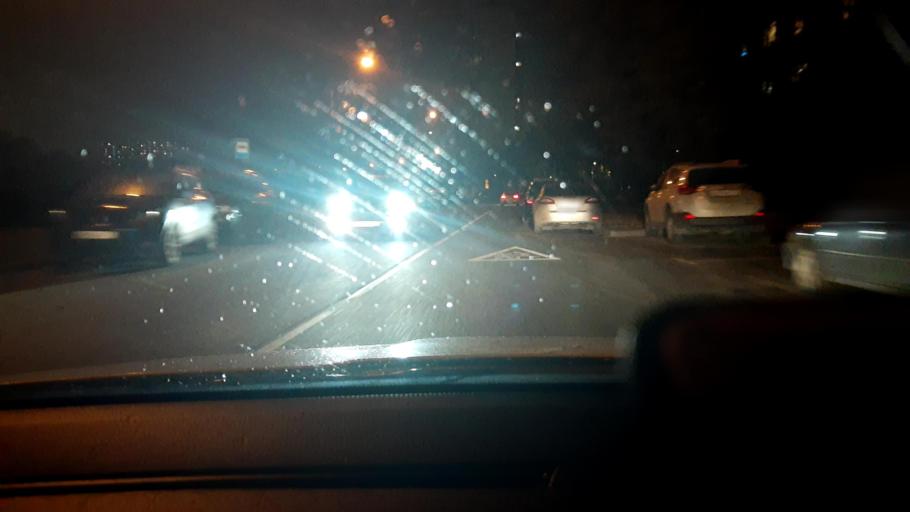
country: RU
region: Moscow
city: Solntsevo
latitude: 55.6464
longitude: 37.3719
